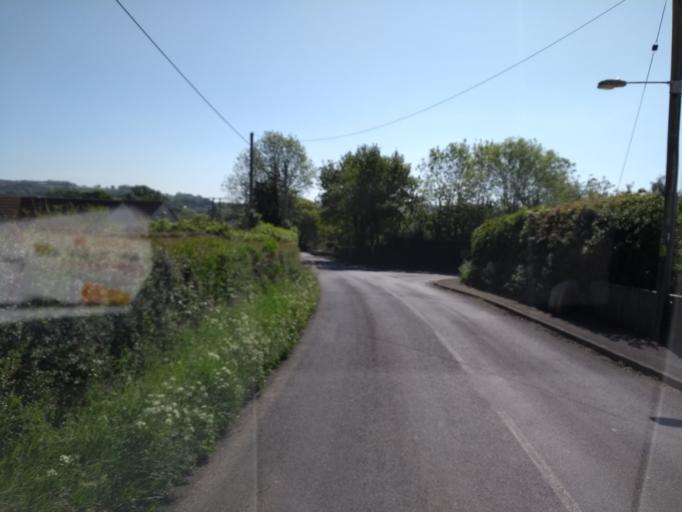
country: GB
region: England
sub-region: Somerset
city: Chard
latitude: 50.8468
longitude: -2.9538
